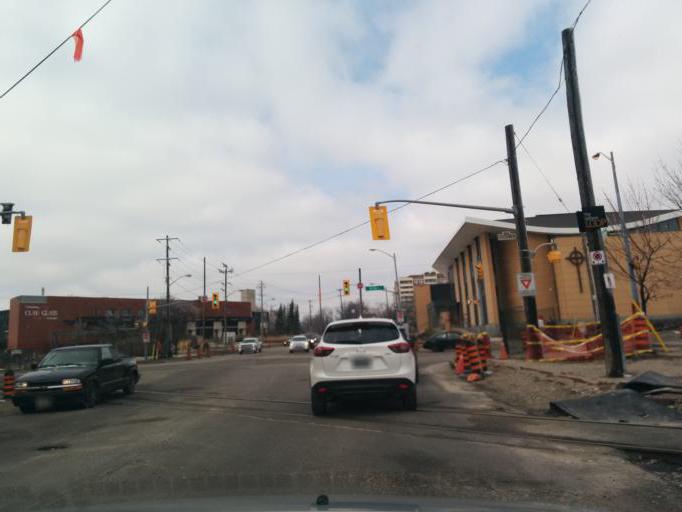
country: CA
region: Ontario
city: Waterloo
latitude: 43.4641
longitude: -80.5249
